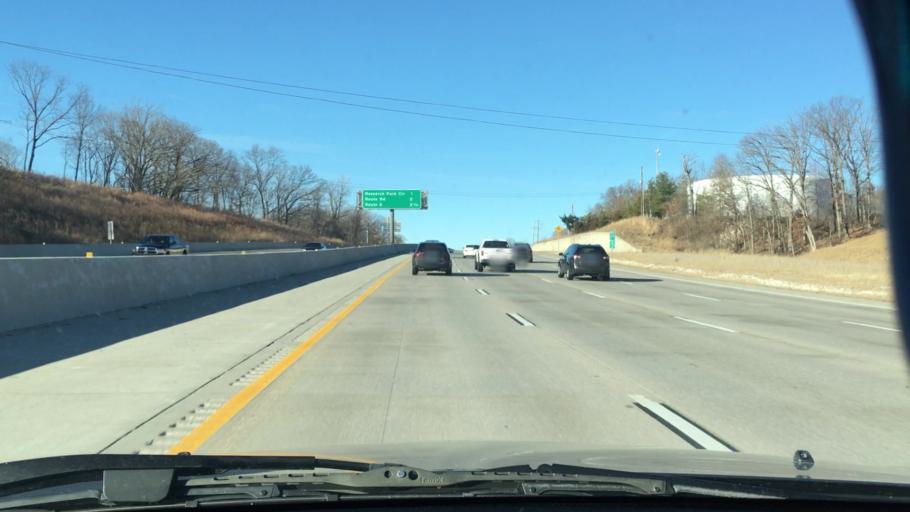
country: US
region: Missouri
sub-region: Saint Charles County
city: Weldon Spring
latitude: 38.6920
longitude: -90.6647
